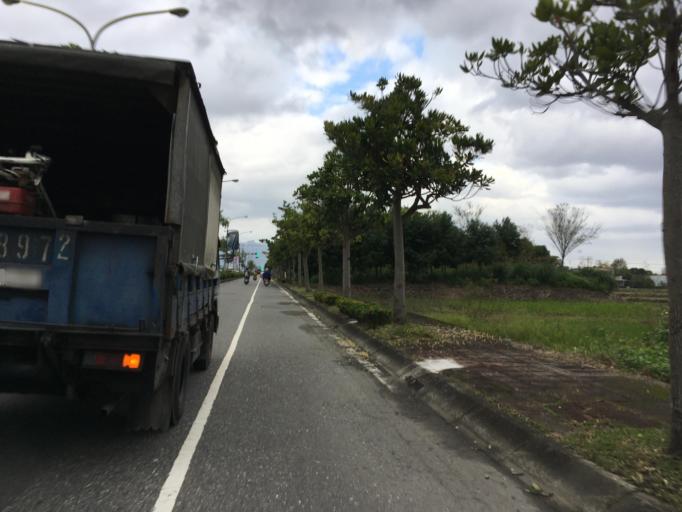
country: TW
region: Taiwan
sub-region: Yilan
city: Yilan
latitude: 24.7419
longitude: 121.7719
